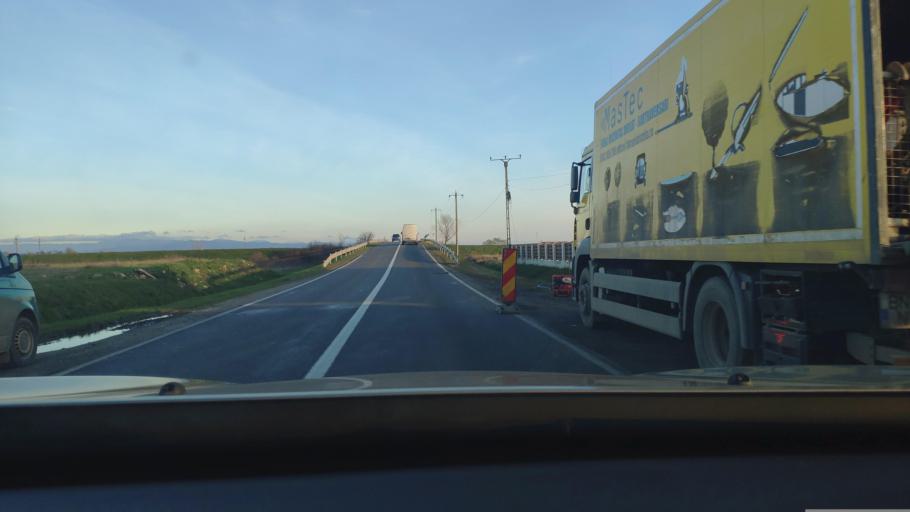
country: RO
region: Satu Mare
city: Culciu Mic
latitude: 47.7849
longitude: 23.0573
